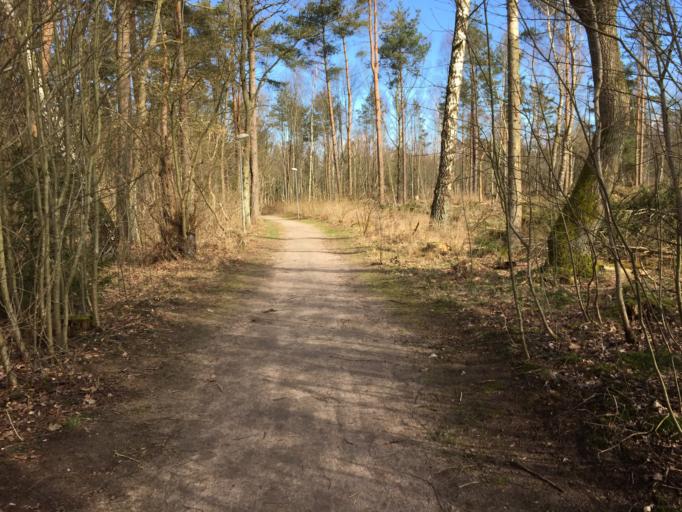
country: SE
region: Skane
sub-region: Lunds Kommun
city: Veberod
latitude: 55.6327
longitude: 13.5103
